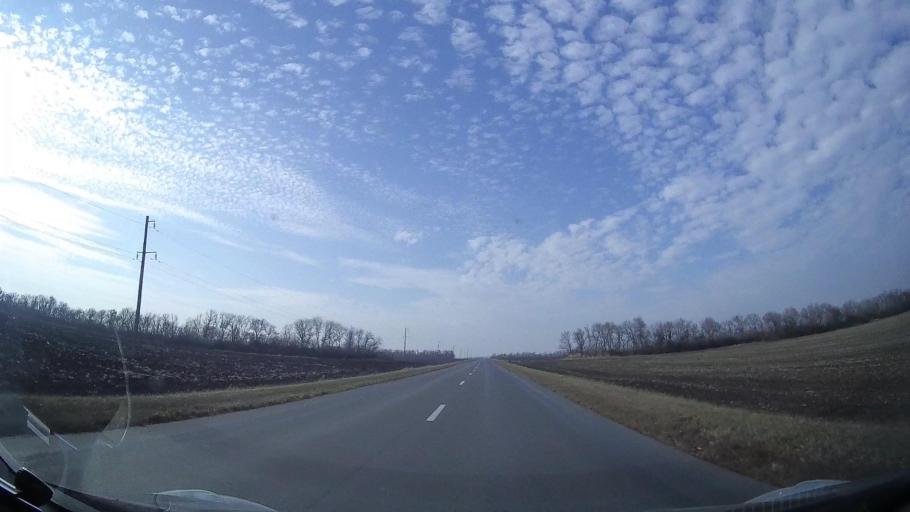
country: RU
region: Rostov
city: Veselyy
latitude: 46.9695
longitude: 40.6660
